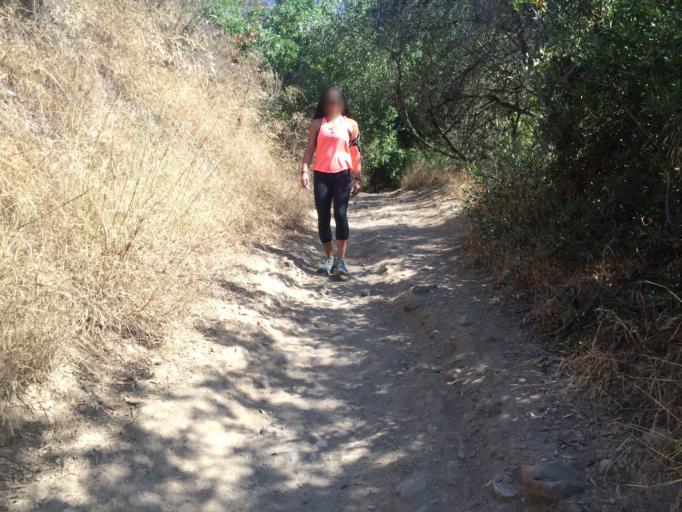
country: US
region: California
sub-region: Los Angeles County
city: Santa Monica
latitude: 34.0596
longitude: -118.5301
